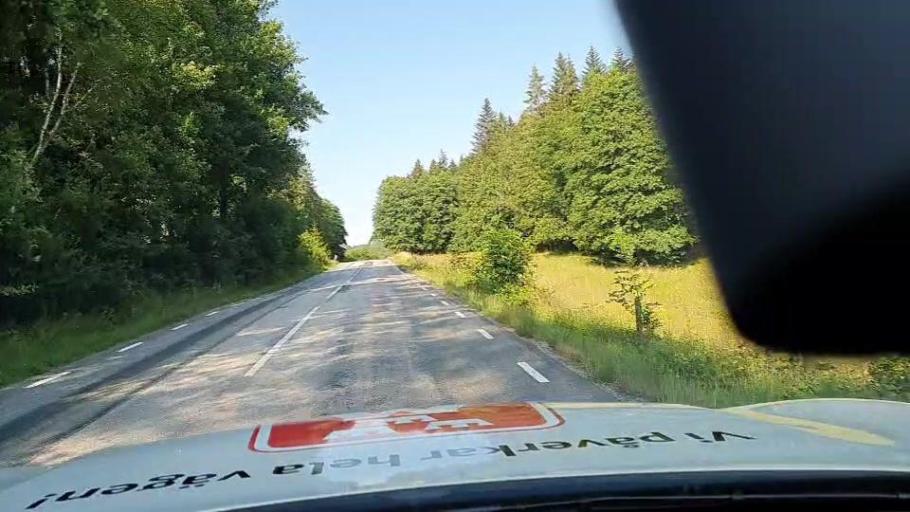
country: SE
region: Vaestra Goetaland
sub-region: Orust
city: Henan
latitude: 58.2173
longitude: 11.5942
